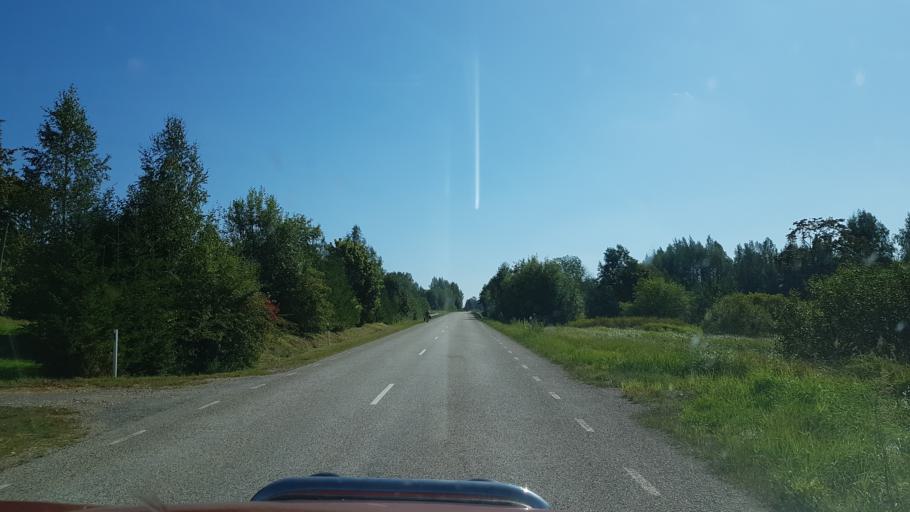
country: EE
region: Polvamaa
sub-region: Polva linn
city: Polva
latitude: 58.2441
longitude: 27.1997
